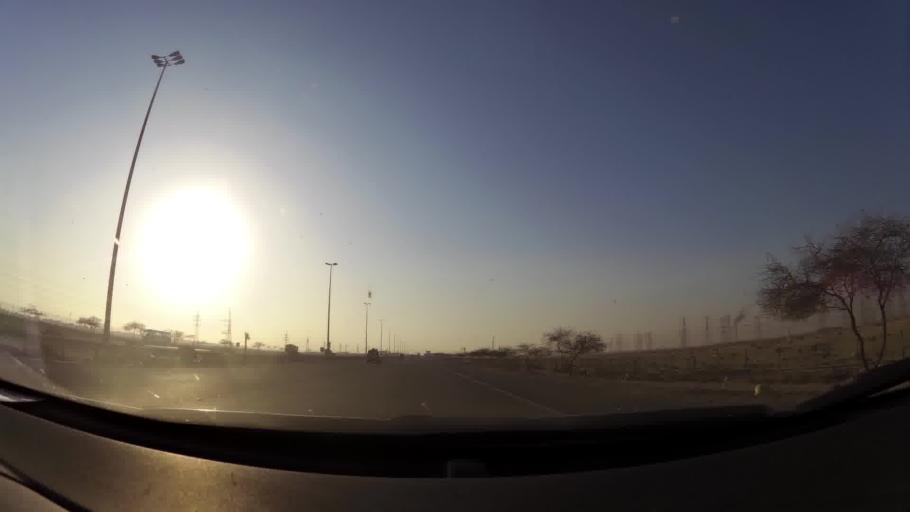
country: KW
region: Al Ahmadi
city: Al Fahahil
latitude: 28.8062
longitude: 48.2671
